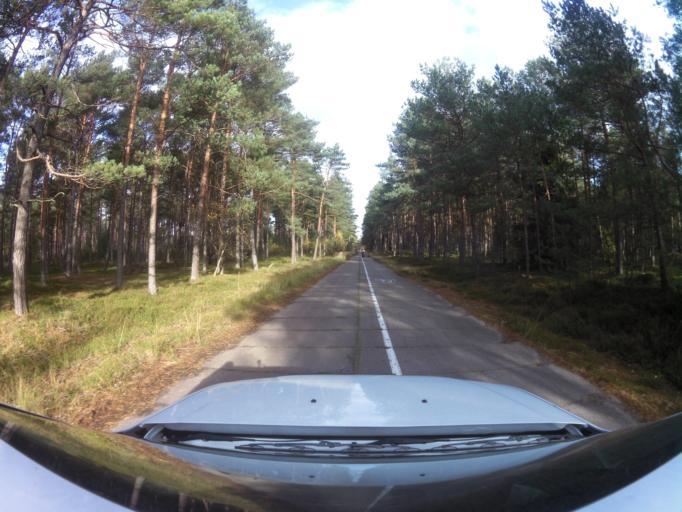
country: PL
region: West Pomeranian Voivodeship
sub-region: Powiat gryficki
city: Cerkwica
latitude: 54.1057
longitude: 15.1485
